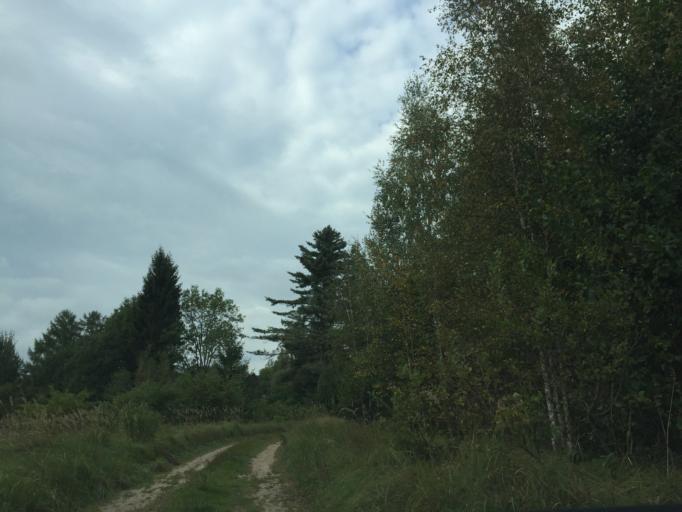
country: LV
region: Baldone
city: Baldone
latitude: 56.7676
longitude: 24.4568
